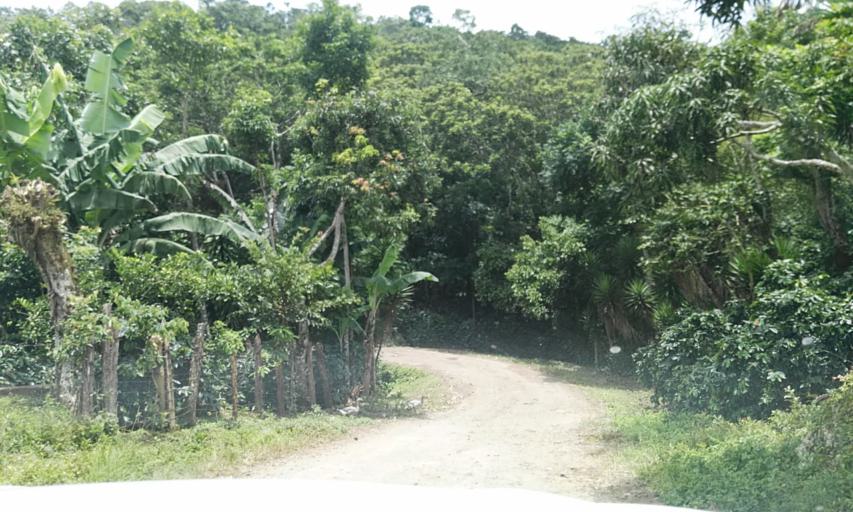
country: NI
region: Matagalpa
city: San Ramon
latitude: 13.0056
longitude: -85.8718
